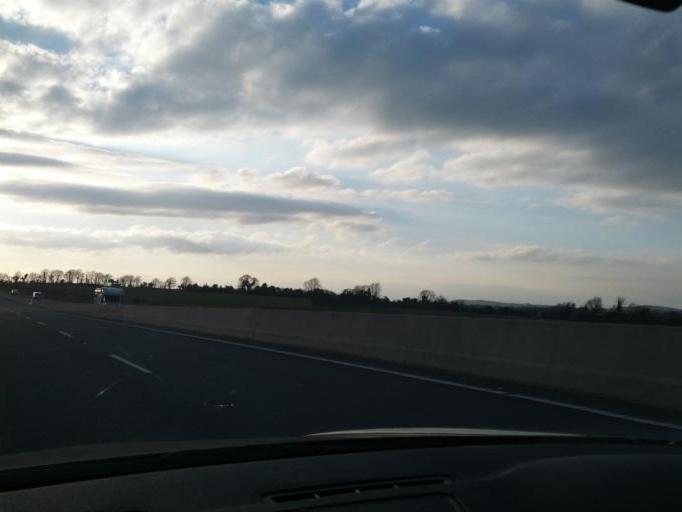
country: IE
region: Munster
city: Nenagh Bridge
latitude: 52.8743
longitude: -8.0361
